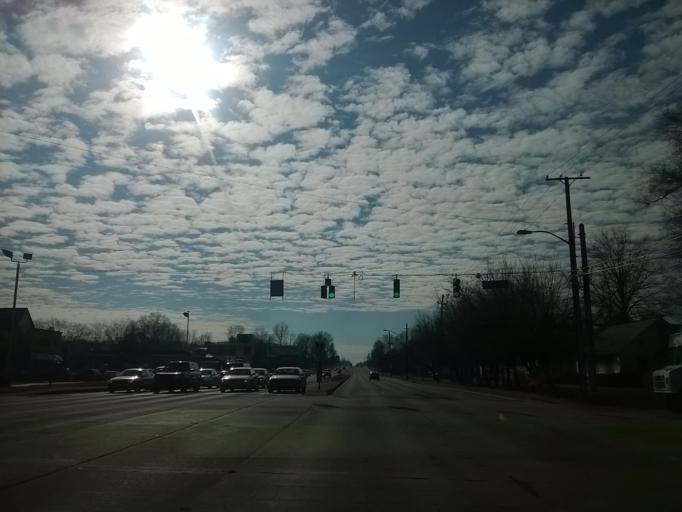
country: US
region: Indiana
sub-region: Marion County
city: Broad Ripple
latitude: 39.8761
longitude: -86.1222
